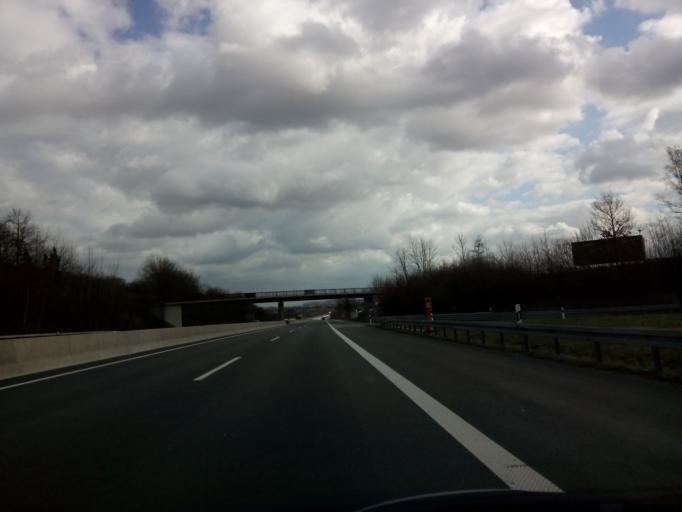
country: DE
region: Lower Saxony
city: Bissendorf
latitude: 52.2434
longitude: 8.1341
